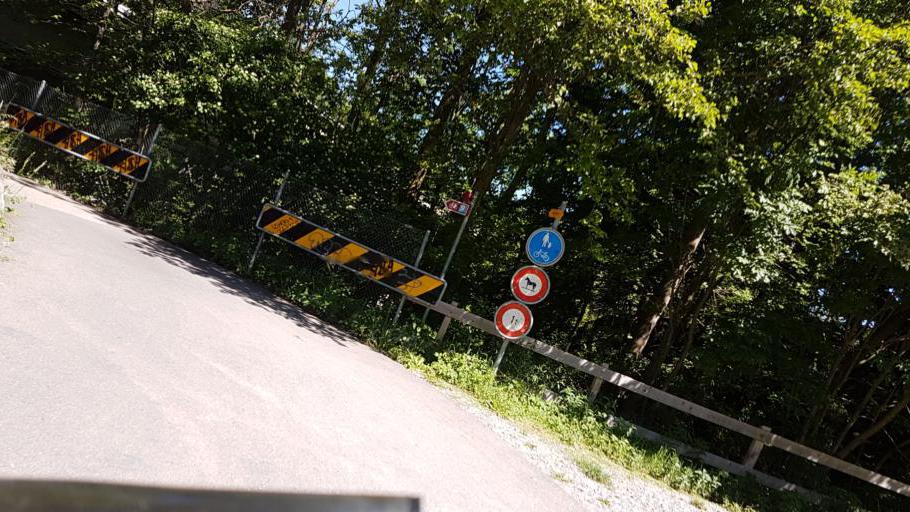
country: CH
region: Bern
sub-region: Frutigen-Niedersimmental District
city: Wimmis
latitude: 46.6867
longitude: 7.6453
